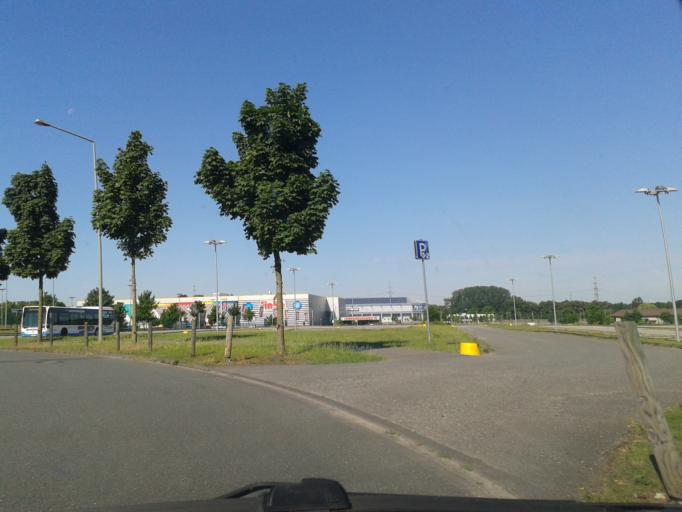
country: DE
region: North Rhine-Westphalia
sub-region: Regierungsbezirk Detmold
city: Paderborn
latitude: 51.7312
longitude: 8.7211
